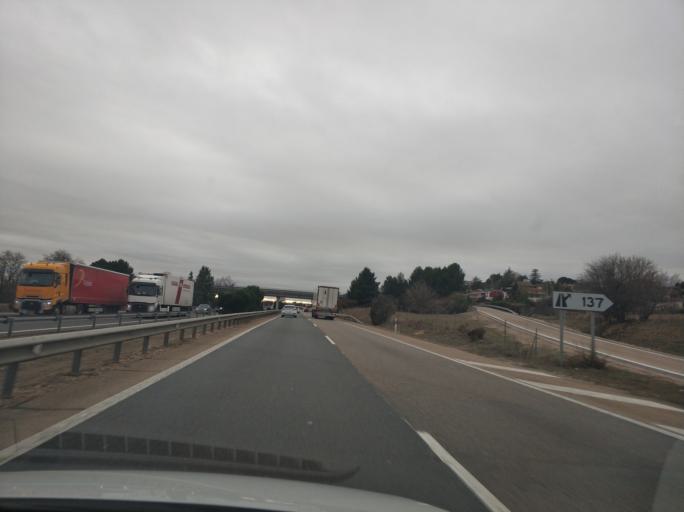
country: ES
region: Castille and Leon
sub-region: Provincia de Valladolid
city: Simancas
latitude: 41.5753
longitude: -4.8483
